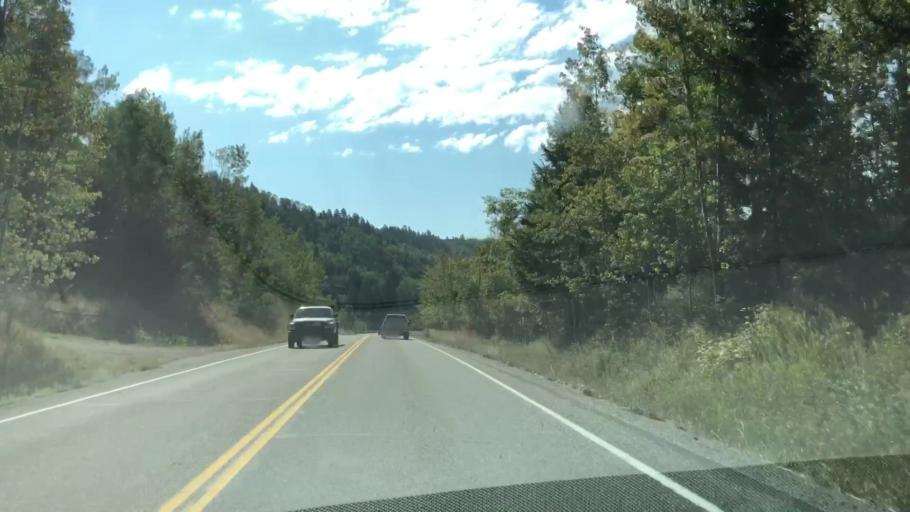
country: US
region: Idaho
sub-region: Teton County
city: Victor
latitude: 43.2801
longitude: -111.1175
